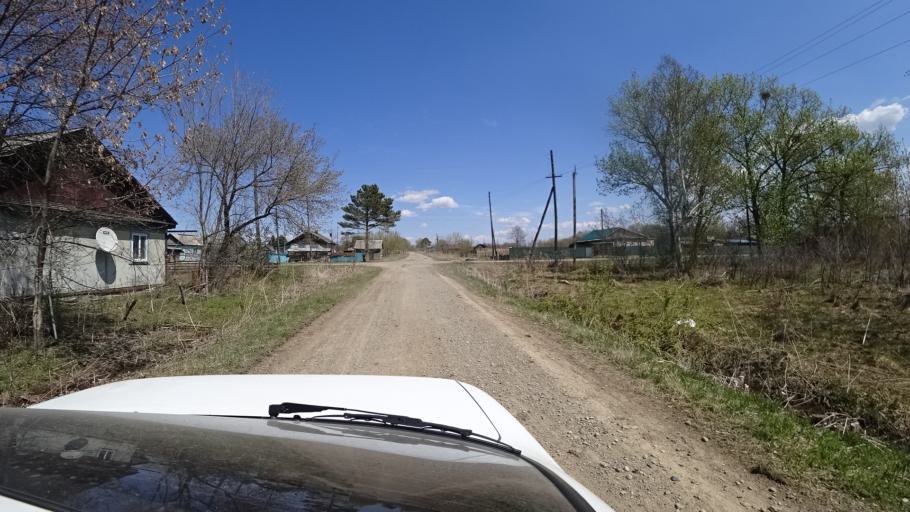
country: RU
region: Primorskiy
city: Lazo
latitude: 45.7914
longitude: 133.7669
